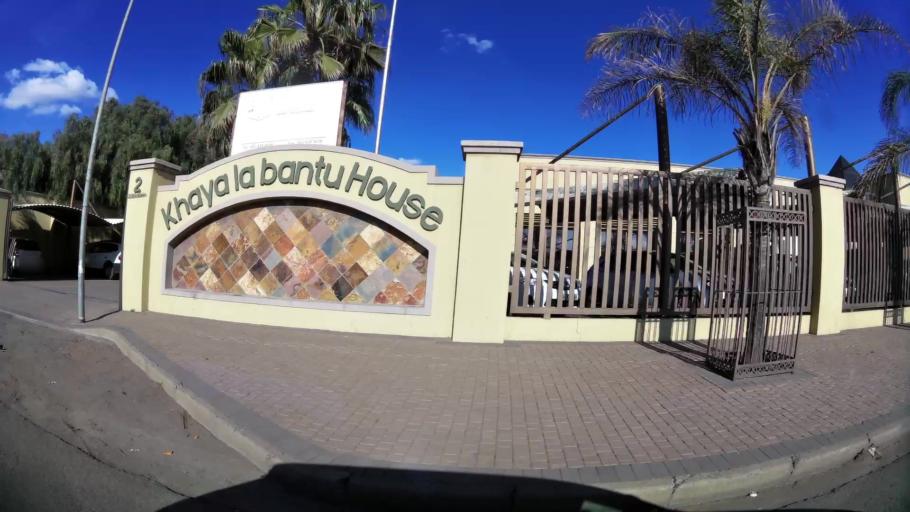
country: ZA
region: Northern Cape
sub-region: Frances Baard District Municipality
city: Kimberley
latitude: -28.7315
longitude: 24.7605
